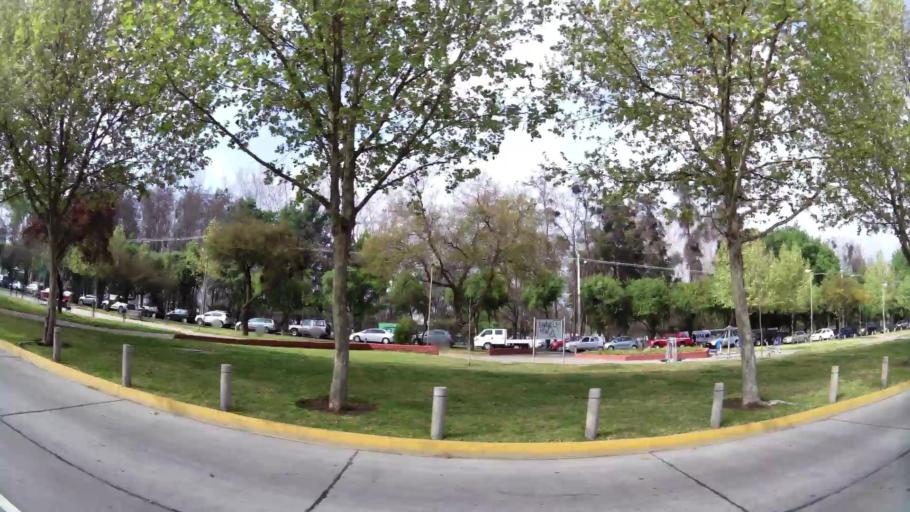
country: CL
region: Santiago Metropolitan
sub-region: Provincia de Santiago
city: Villa Presidente Frei, Nunoa, Santiago, Chile
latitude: -33.4295
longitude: -70.5463
